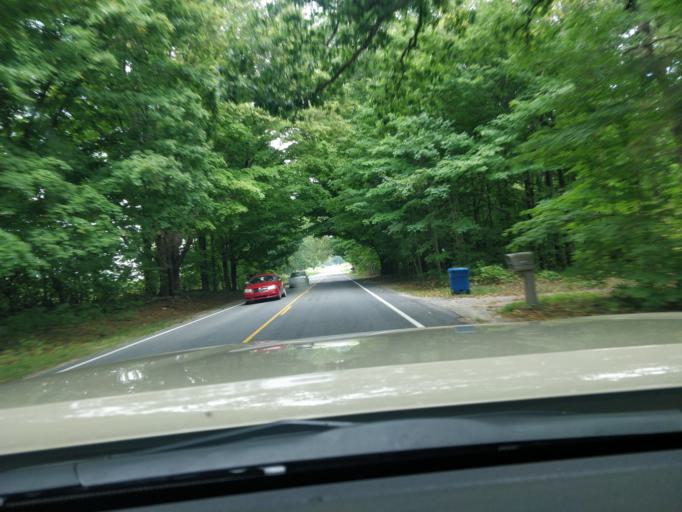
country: US
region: Michigan
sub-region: Kent County
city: Lowell
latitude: 42.8860
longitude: -85.2866
